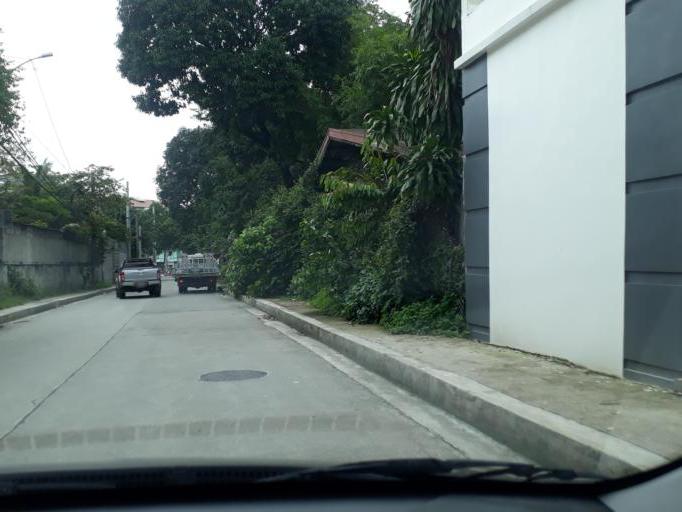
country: PH
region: Metro Manila
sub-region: San Juan
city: San Juan
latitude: 14.6194
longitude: 121.0412
